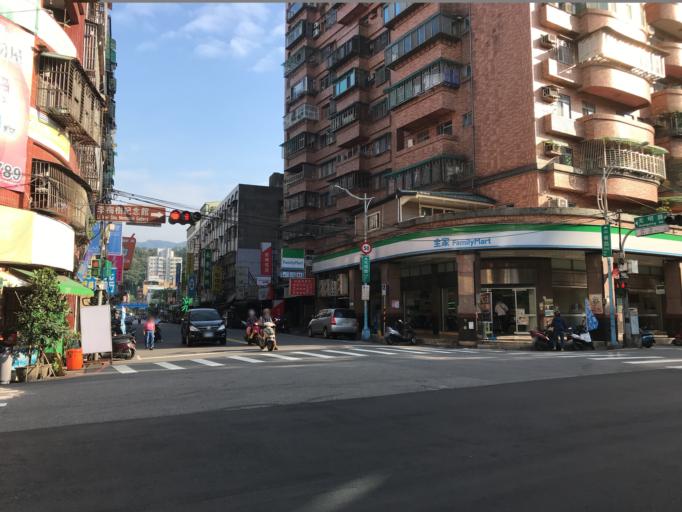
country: TW
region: Taiwan
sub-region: Taoyuan
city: Taoyuan
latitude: 24.9316
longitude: 121.3730
